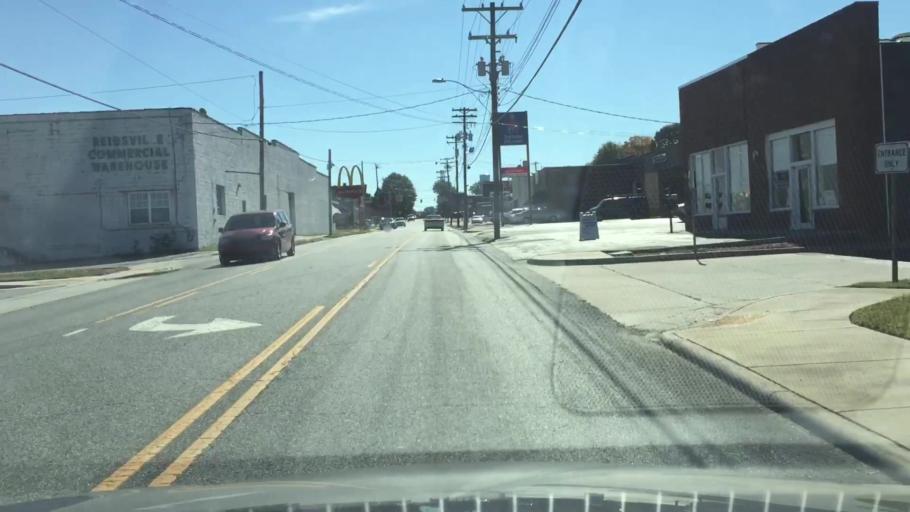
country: US
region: North Carolina
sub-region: Rockingham County
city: Reidsville
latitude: 36.3544
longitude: -79.6647
